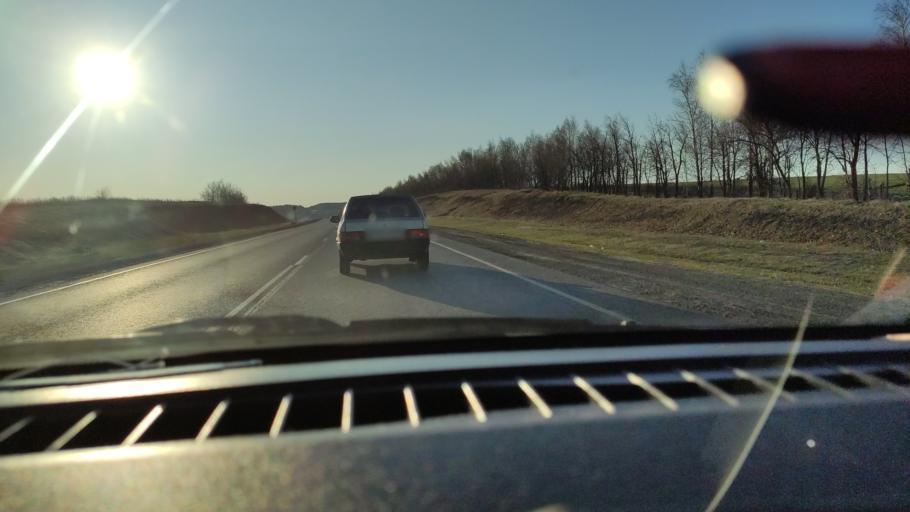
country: RU
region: Saratov
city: Shikhany
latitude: 52.1167
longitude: 47.2830
